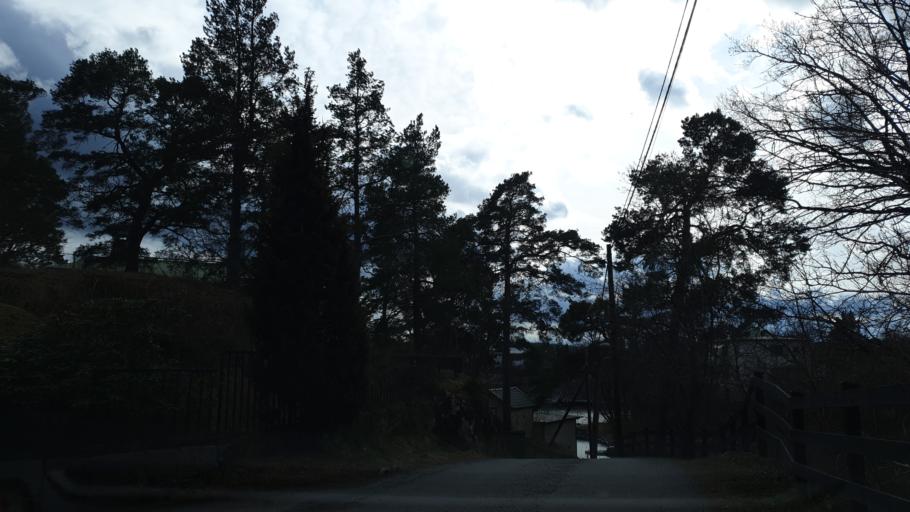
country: SE
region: Stockholm
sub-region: Nacka Kommun
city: Saltsjobaden
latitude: 59.2679
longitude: 18.3125
